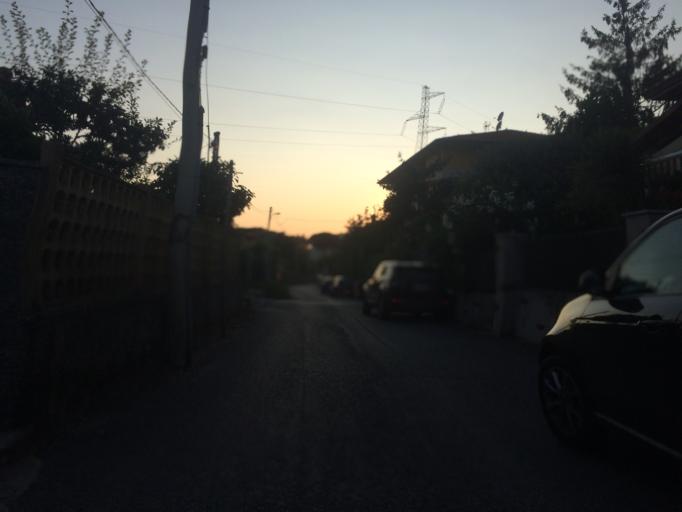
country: IT
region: Tuscany
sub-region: Provincia di Massa-Carrara
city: Massa
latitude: 44.0398
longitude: 10.1178
